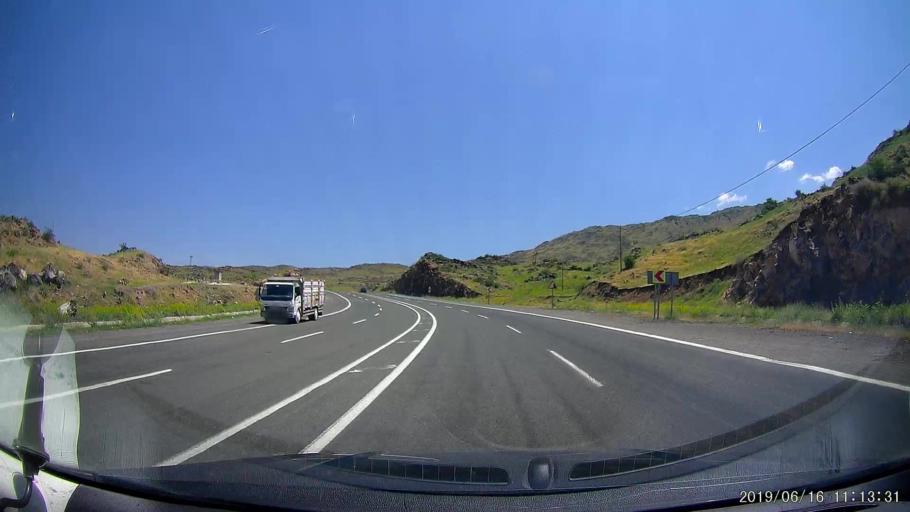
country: TR
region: Igdir
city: Igdir
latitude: 39.7843
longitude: 44.1395
